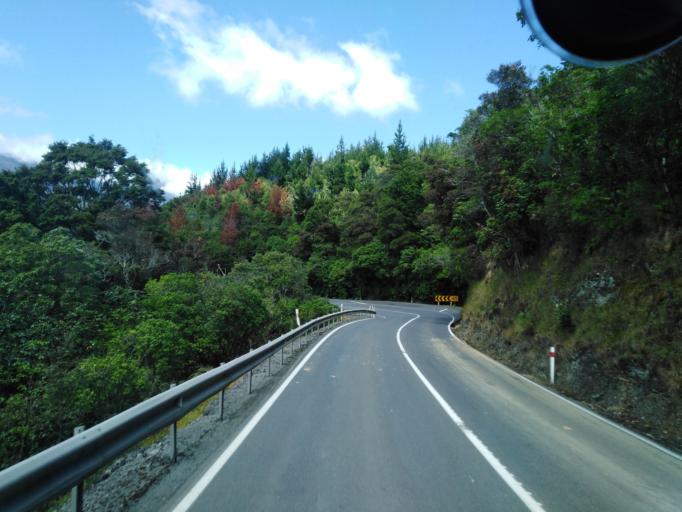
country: NZ
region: Nelson
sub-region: Nelson City
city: Nelson
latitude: -41.2237
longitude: 173.4358
